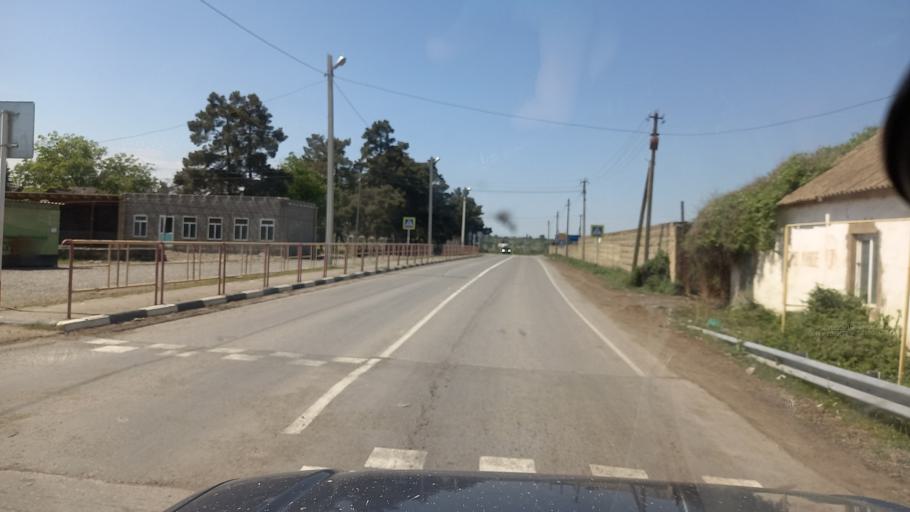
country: AZ
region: Qusar
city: Samur
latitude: 41.7258
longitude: 48.4576
